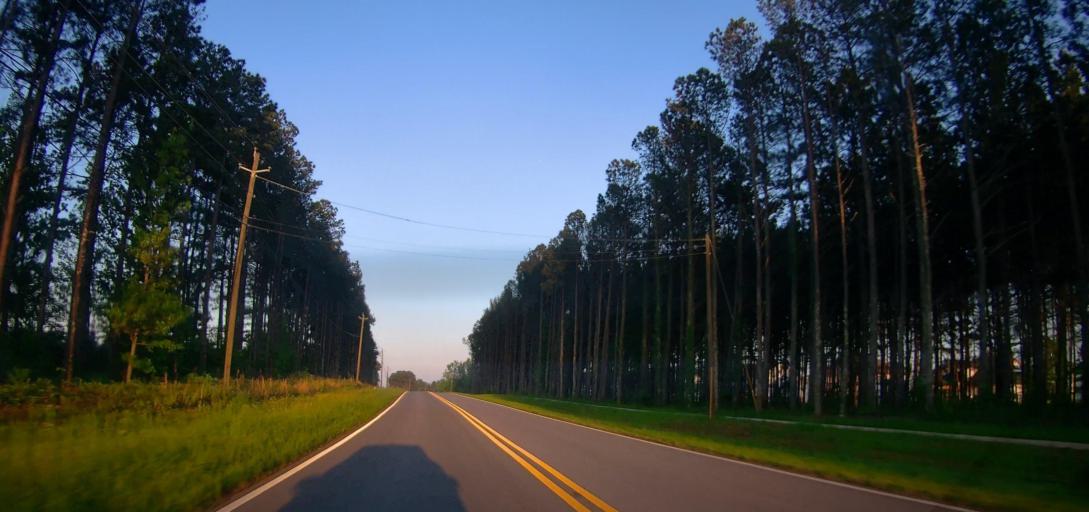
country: US
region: Georgia
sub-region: Henry County
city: McDonough
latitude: 33.4034
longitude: -84.1252
